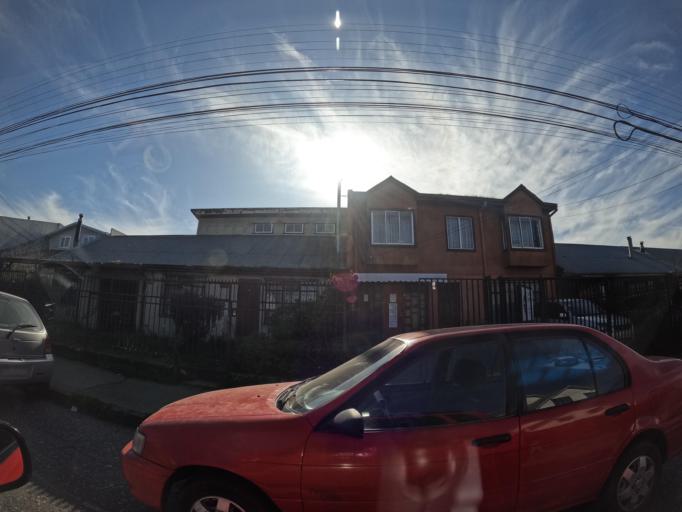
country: CL
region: Biobio
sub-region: Provincia de Concepcion
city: Concepcion
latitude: -36.8067
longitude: -73.0763
